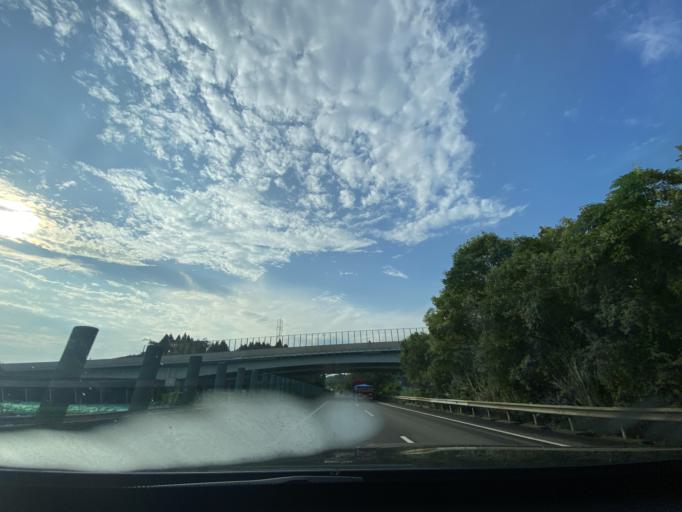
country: CN
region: Sichuan
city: Jiancheng
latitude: 30.3200
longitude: 104.5740
